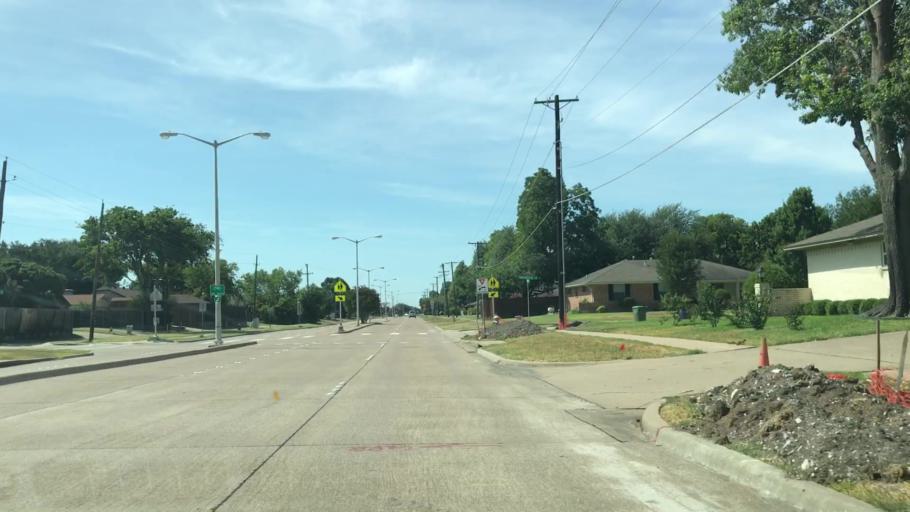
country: US
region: Texas
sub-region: Dallas County
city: Garland
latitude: 32.9381
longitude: -96.6400
